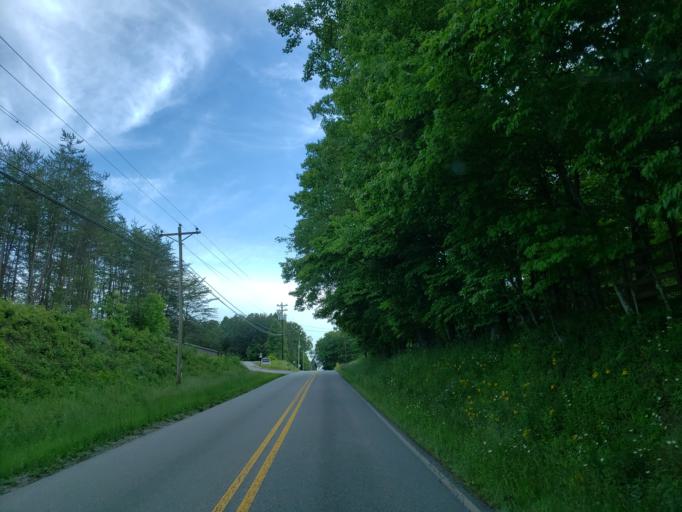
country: US
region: Georgia
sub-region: Fannin County
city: Blue Ridge
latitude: 34.8459
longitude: -84.3391
